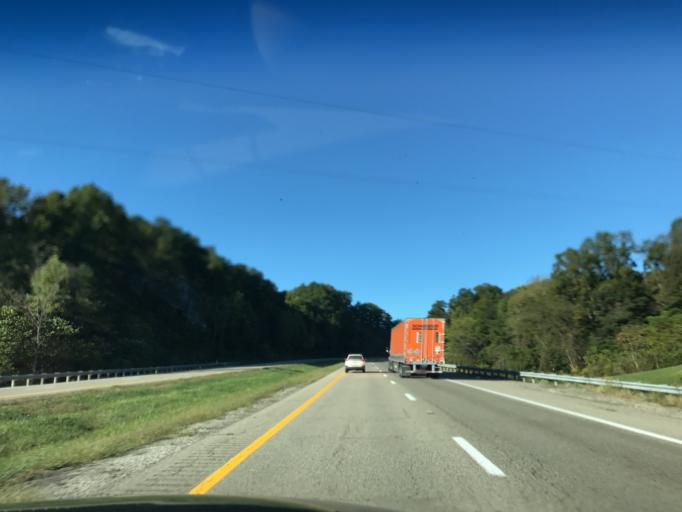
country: US
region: Ohio
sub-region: Washington County
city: Newport
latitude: 39.2516
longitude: -81.2551
